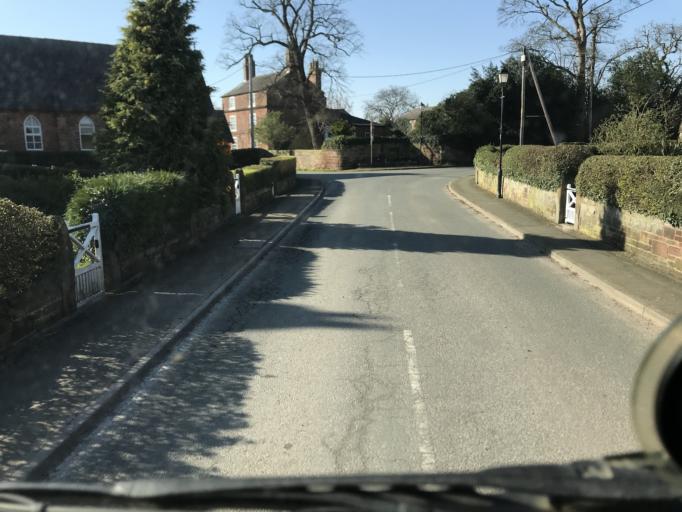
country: GB
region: England
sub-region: Cheshire West and Chester
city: Waverton
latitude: 53.1528
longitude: -2.8328
